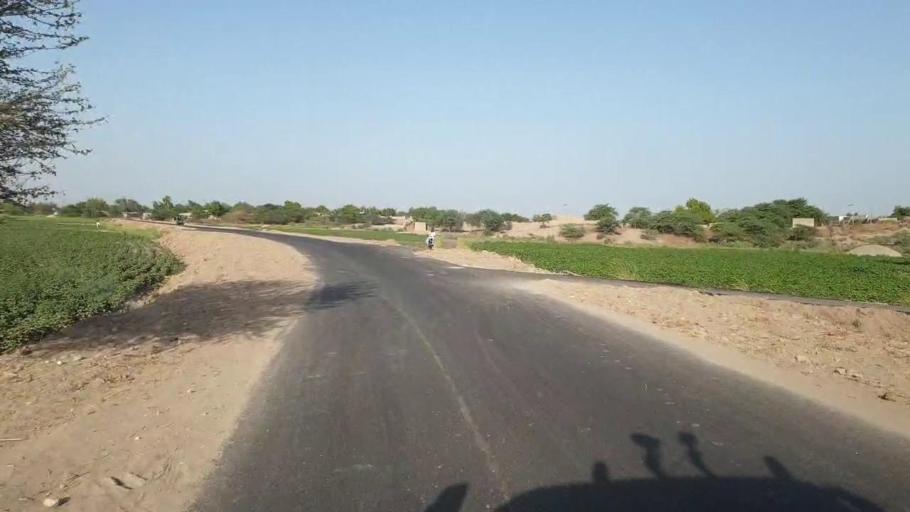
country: PK
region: Sindh
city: Jam Sahib
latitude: 26.3475
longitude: 68.5588
